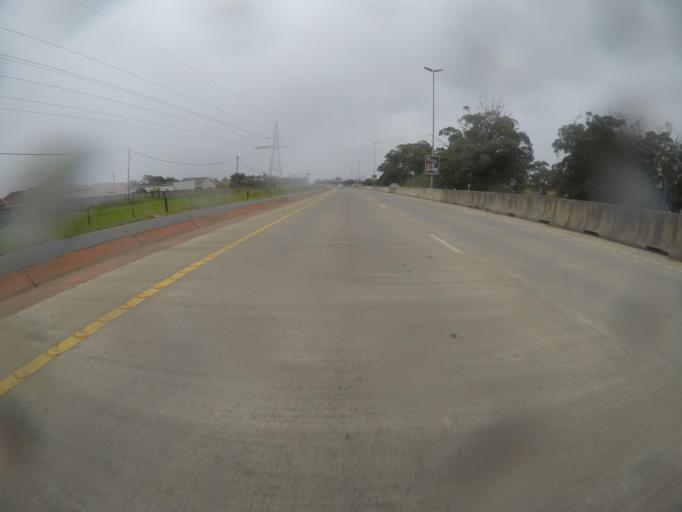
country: ZA
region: Eastern Cape
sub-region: Buffalo City Metropolitan Municipality
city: East London
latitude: -32.9355
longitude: 27.9894
